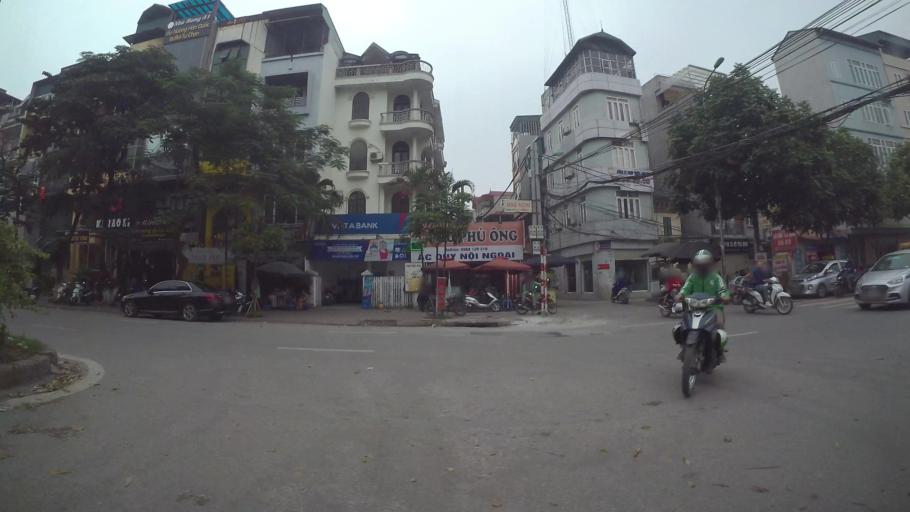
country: VN
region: Ha Noi
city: Hai BaTrung
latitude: 20.9837
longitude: 105.8439
